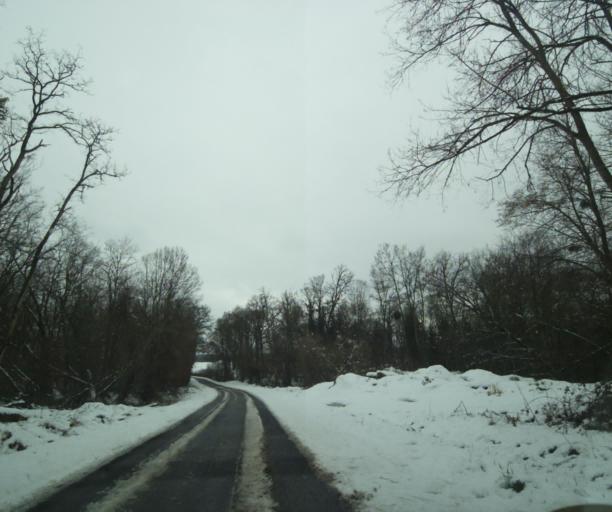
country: FR
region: Champagne-Ardenne
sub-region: Departement de la Haute-Marne
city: Montier-en-Der
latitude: 48.4218
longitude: 4.7288
